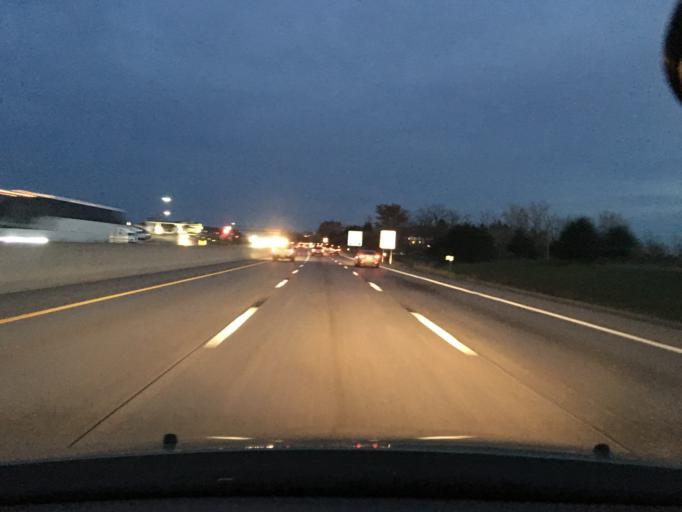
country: US
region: New York
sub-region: Ontario County
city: Victor
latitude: 42.9990
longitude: -77.4179
